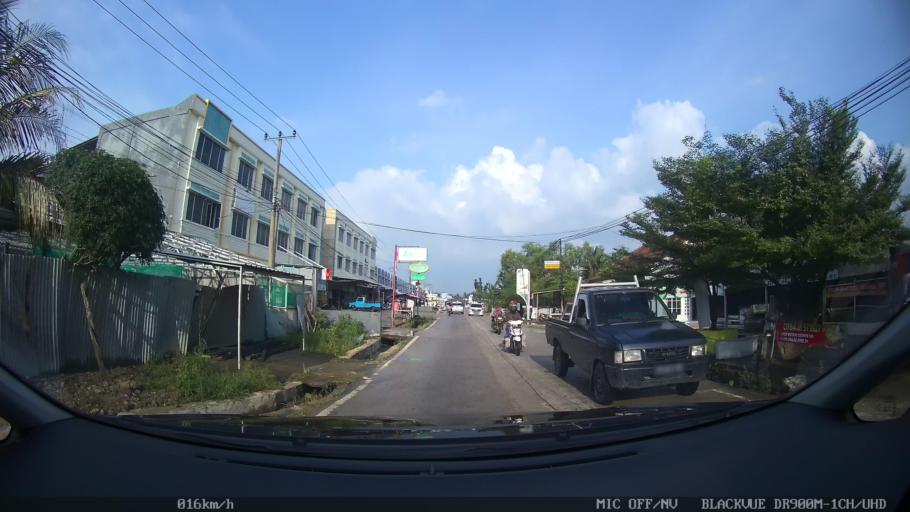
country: ID
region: Lampung
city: Kedaton
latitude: -5.3857
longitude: 105.3126
